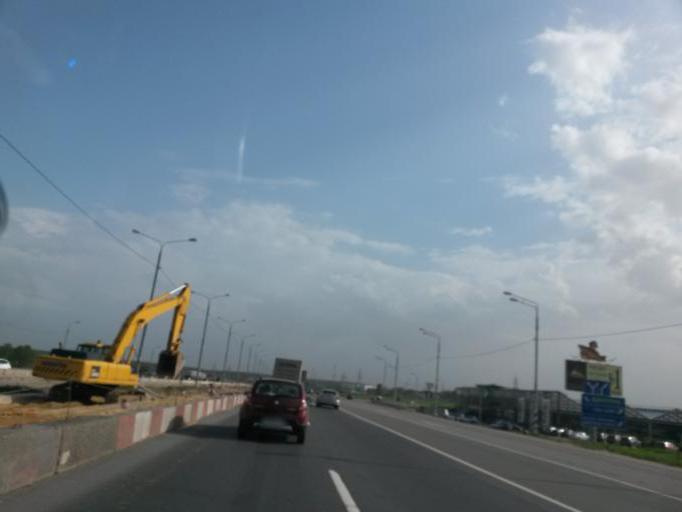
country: RU
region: Moskovskaya
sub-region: Podol'skiy Rayon
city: Podol'sk
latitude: 55.3918
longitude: 37.6047
